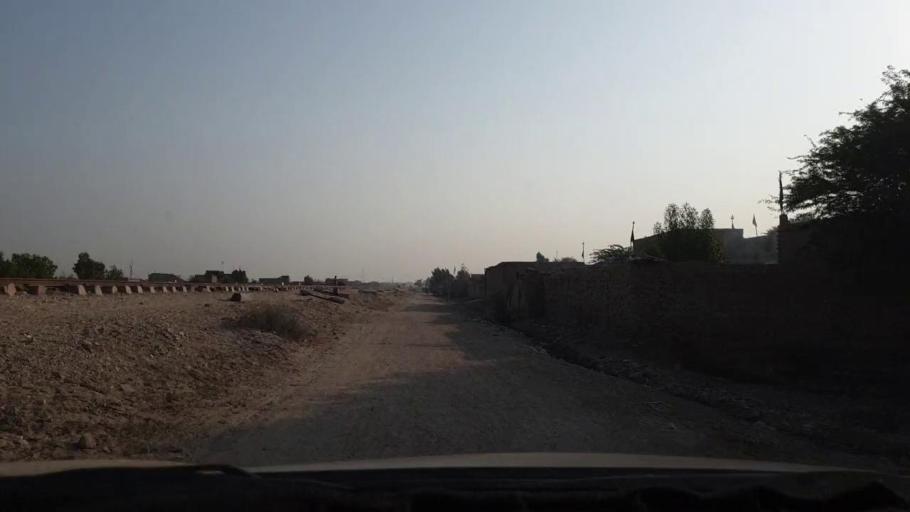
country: PK
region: Sindh
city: Larkana
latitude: 27.5290
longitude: 68.1986
